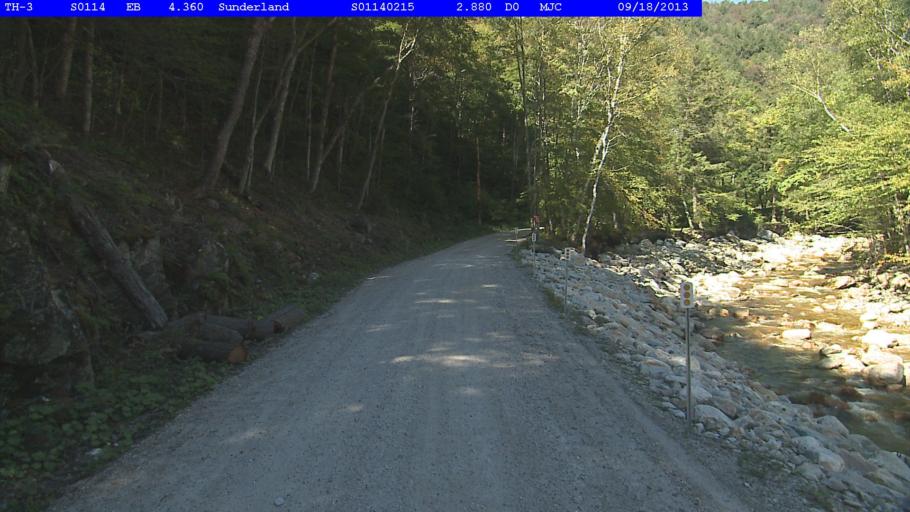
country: US
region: Vermont
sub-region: Bennington County
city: Arlington
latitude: 43.0415
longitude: -73.1033
